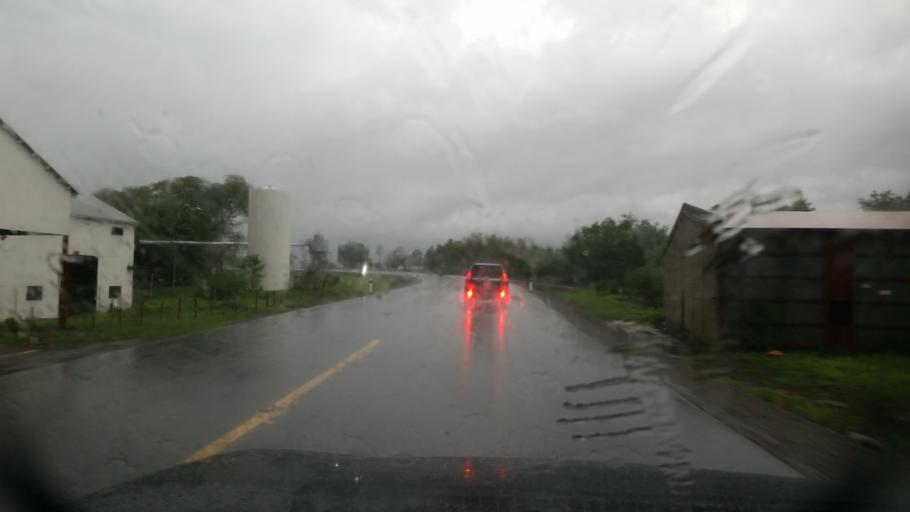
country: NI
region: Chinandega
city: Chichigalpa
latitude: 12.7858
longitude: -86.9371
